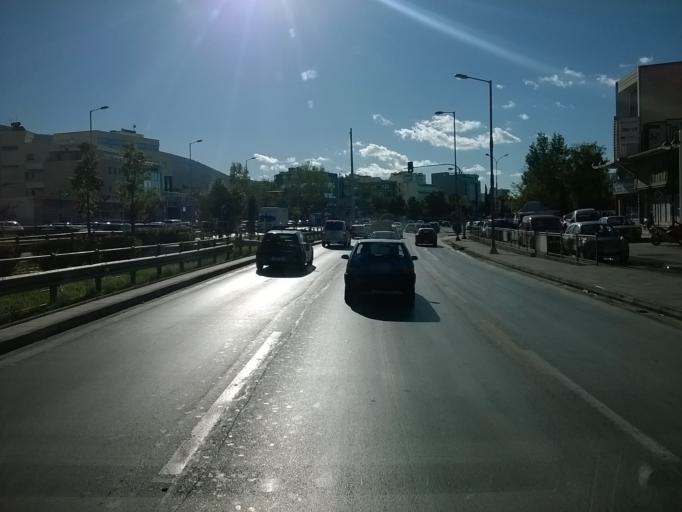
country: GR
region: Attica
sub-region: Nomarchia Athinas
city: Agios Dimitrios
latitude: 37.9352
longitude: 23.7436
